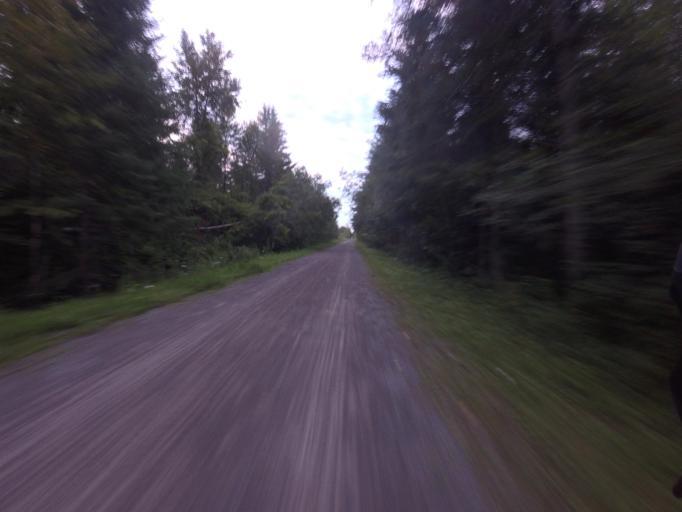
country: CA
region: Ontario
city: Bells Corners
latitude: 45.2329
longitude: -75.9610
